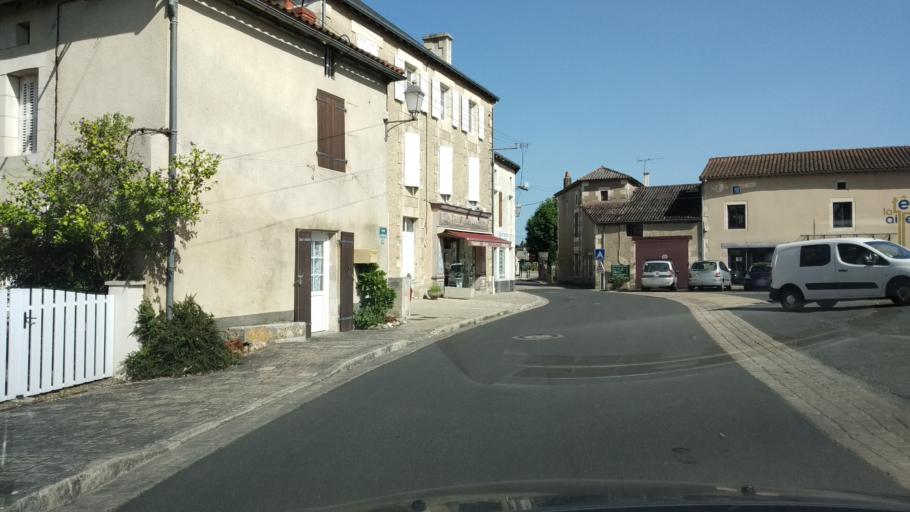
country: FR
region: Poitou-Charentes
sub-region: Departement de la Vienne
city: Lussac-les-Chateaux
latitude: 46.4450
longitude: 0.6646
